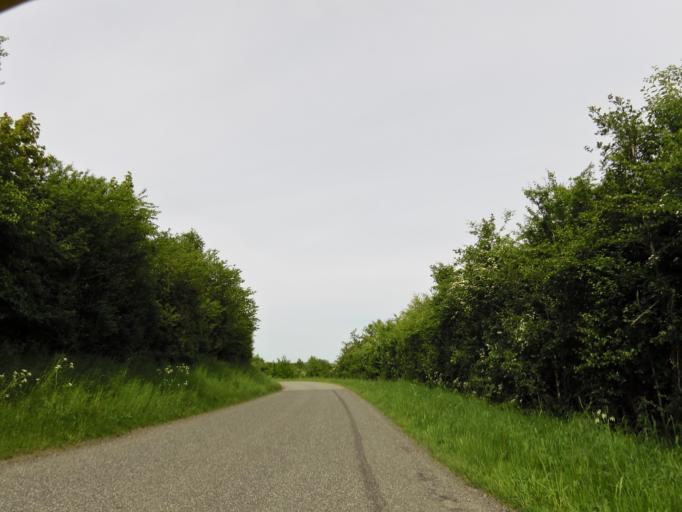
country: DK
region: Central Jutland
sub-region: Holstebro Kommune
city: Vinderup
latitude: 56.5464
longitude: 8.8874
